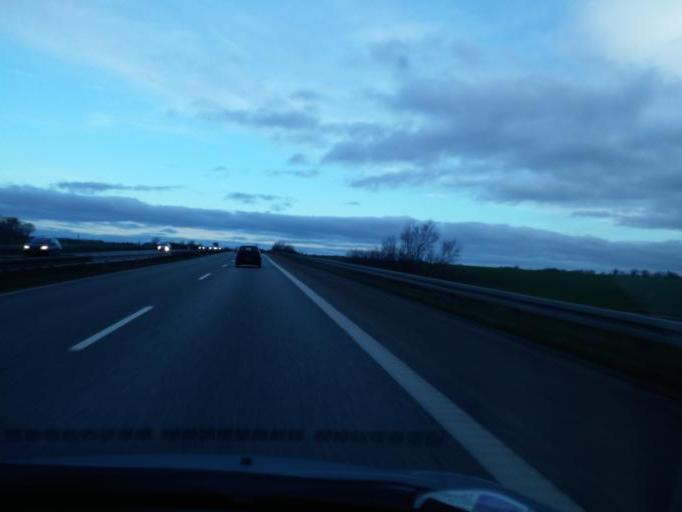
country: DK
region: South Denmark
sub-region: Fredericia Kommune
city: Taulov
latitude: 55.5719
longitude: 9.6158
